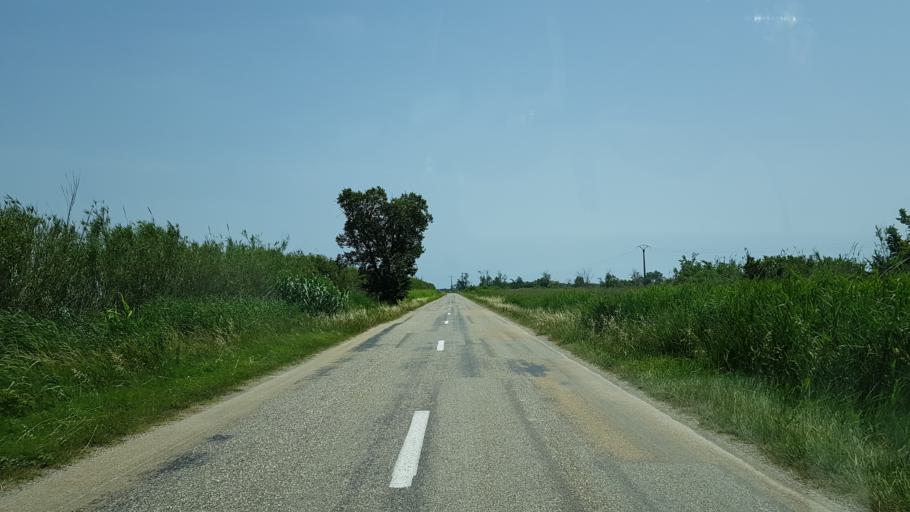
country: FR
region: Provence-Alpes-Cote d'Azur
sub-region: Departement des Bouches-du-Rhone
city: Port-Saint-Louis-du-Rhone
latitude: 43.4468
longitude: 4.6631
